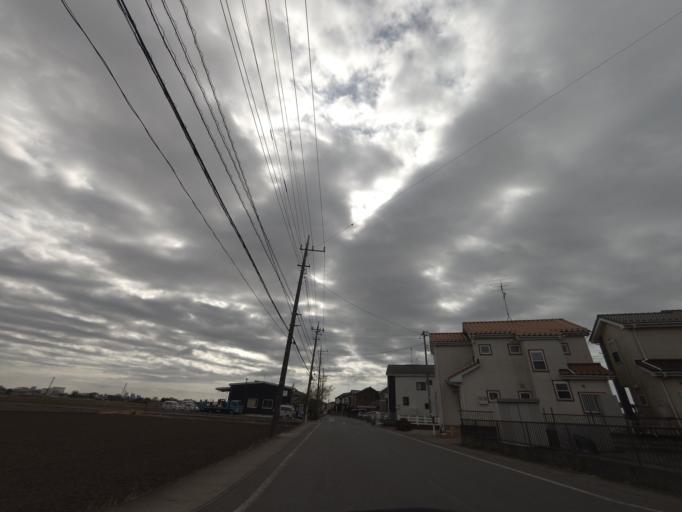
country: JP
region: Saitama
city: Kamifukuoka
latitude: 35.8928
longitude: 139.5388
